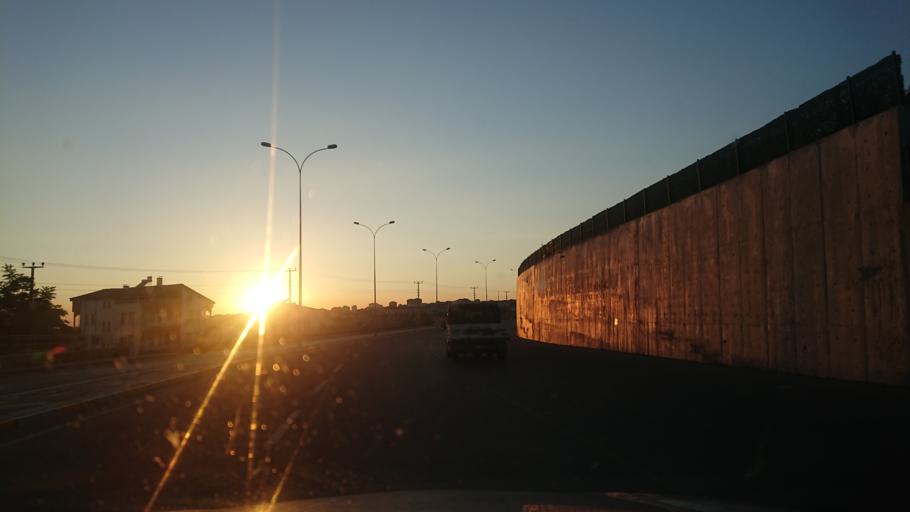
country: TR
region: Aksaray
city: Aksaray
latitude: 38.4033
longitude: 34.0148
